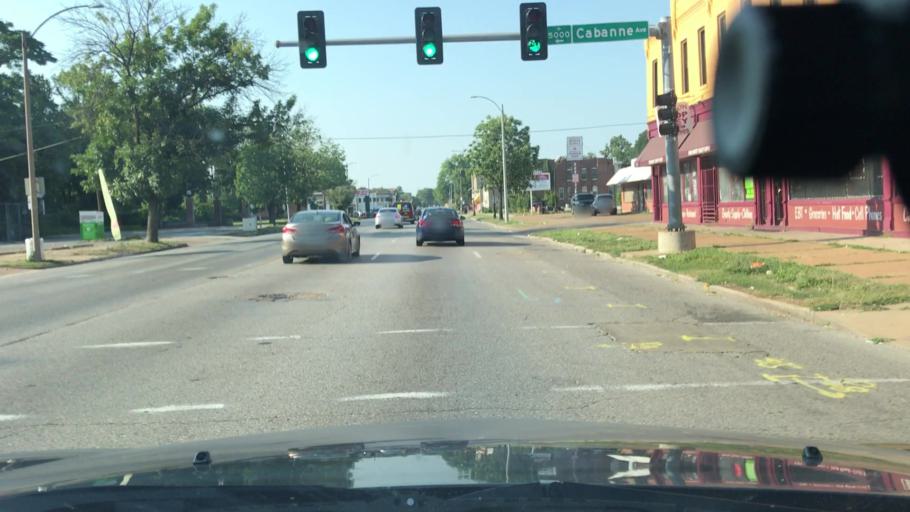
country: US
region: Missouri
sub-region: Saint Louis County
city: Hillsdale
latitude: 38.6560
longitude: -90.2627
